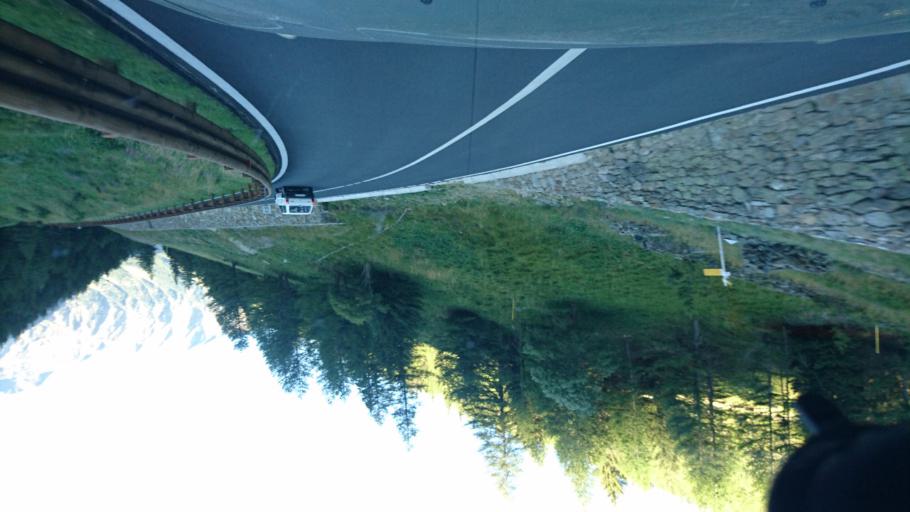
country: IT
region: Aosta Valley
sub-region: Valle d'Aosta
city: San Leonardo
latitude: 45.8428
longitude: 7.1794
